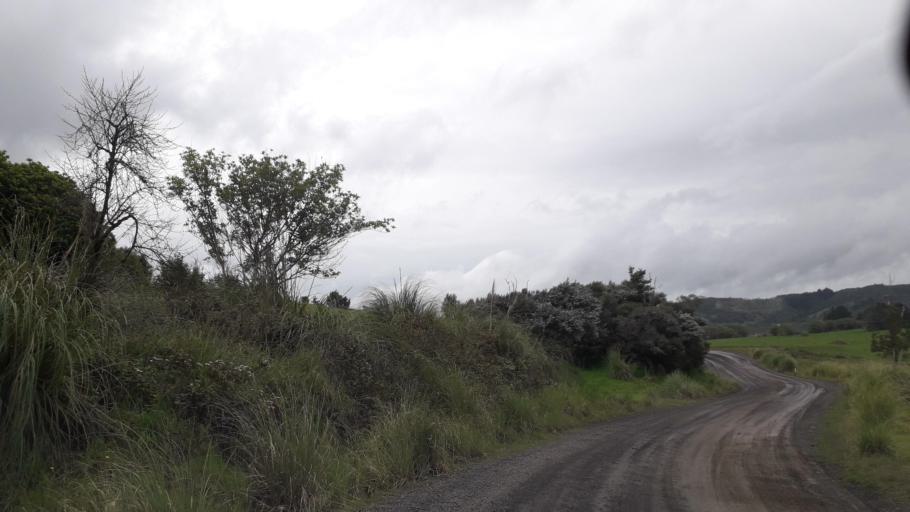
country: NZ
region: Northland
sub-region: Far North District
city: Kaitaia
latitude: -35.4073
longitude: 173.3633
